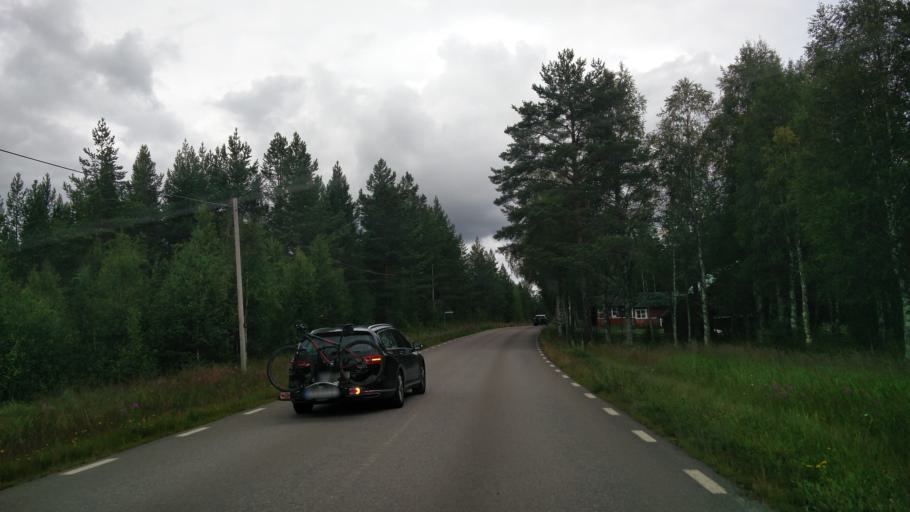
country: NO
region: Hedmark
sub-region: Trysil
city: Innbygda
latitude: 61.1683
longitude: 12.8386
